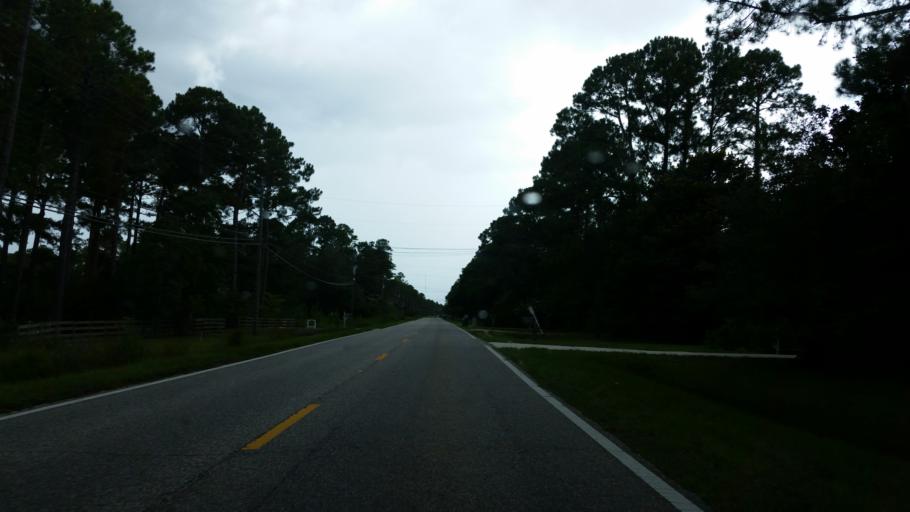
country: US
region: Florida
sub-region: Santa Rosa County
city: Woodlawn Beach
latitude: 30.4293
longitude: -86.9661
